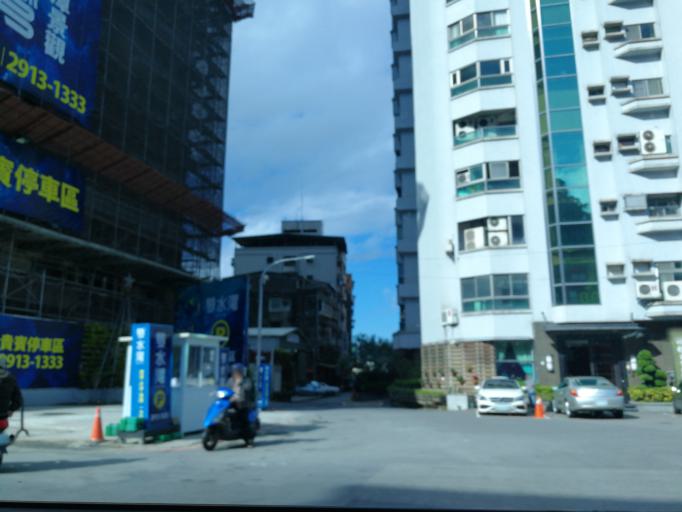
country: TW
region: Taipei
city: Taipei
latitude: 24.9613
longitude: 121.5388
